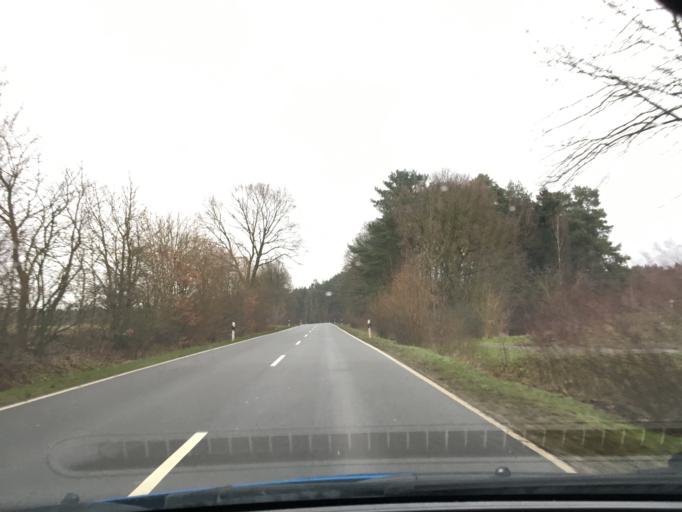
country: DE
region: Schleswig-Holstein
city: Roseburg
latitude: 53.5359
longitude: 10.6317
